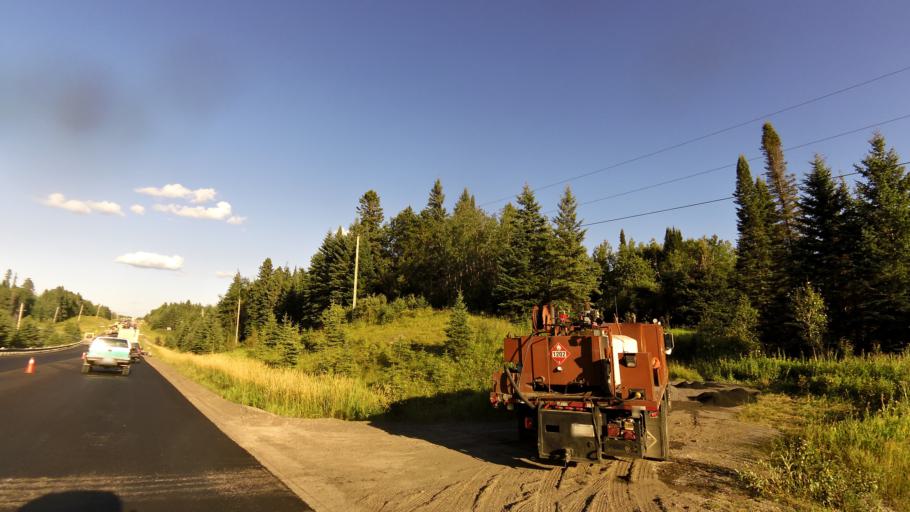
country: CA
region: Ontario
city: Dryden
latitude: 49.8151
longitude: -92.8774
